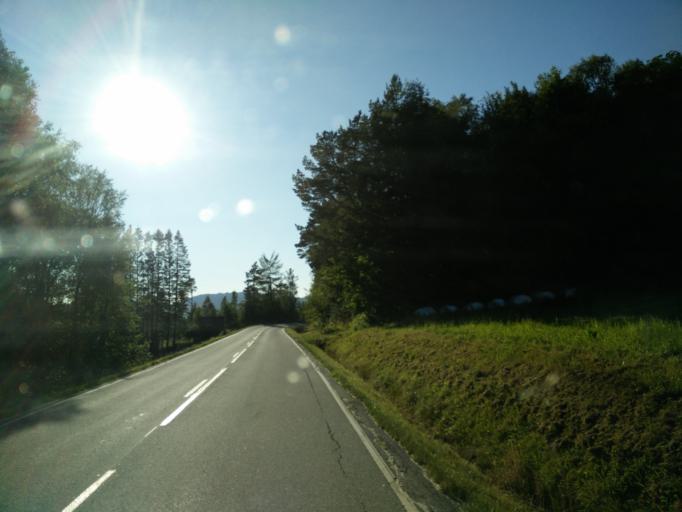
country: NO
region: More og Romsdal
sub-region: Halsa
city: Liaboen
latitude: 63.0847
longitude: 8.3981
